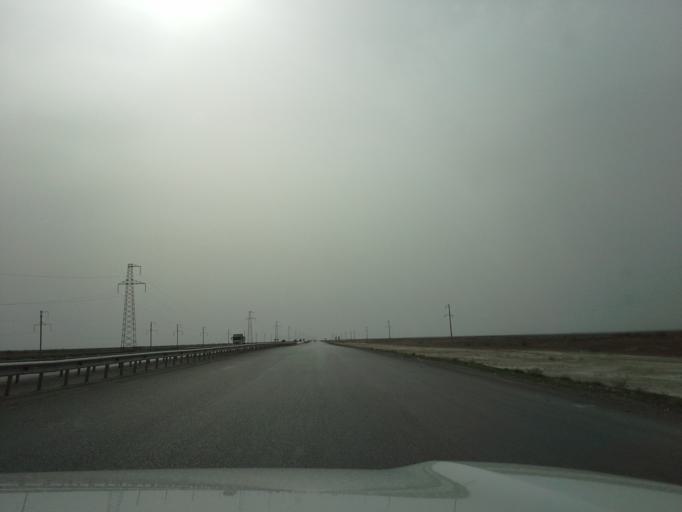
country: TM
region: Ahal
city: Kaka
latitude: 37.5326
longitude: 59.4118
